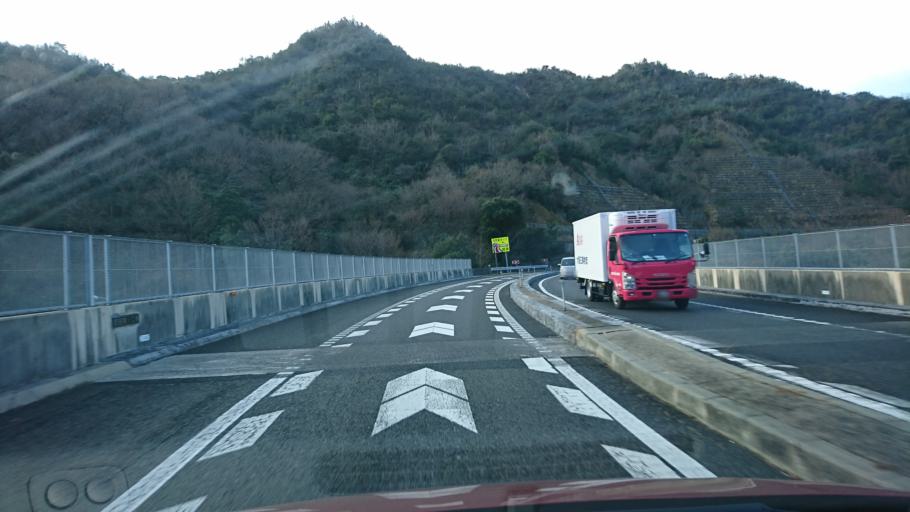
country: JP
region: Hyogo
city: Himeji
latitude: 34.8514
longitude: 134.7412
